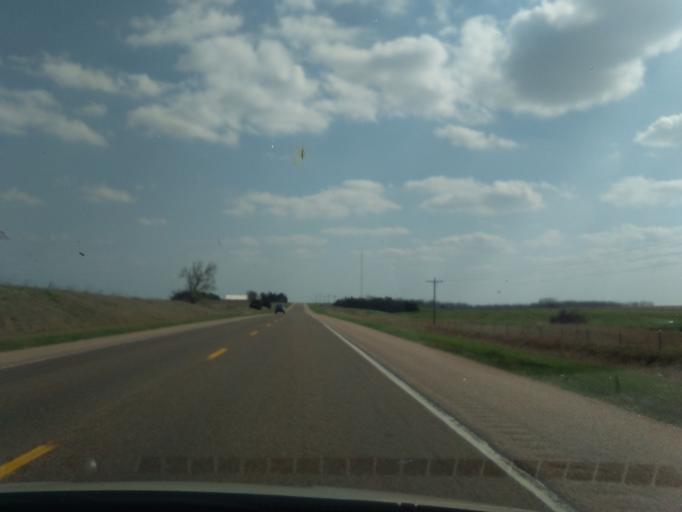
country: US
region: Nebraska
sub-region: Nuckolls County
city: Nelson
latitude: 40.1319
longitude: -98.0670
